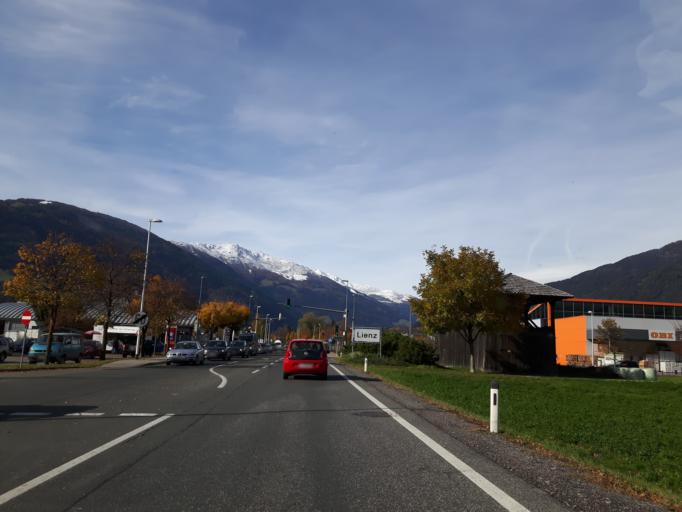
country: AT
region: Tyrol
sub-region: Politischer Bezirk Lienz
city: Lienz
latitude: 46.8314
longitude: 12.7830
